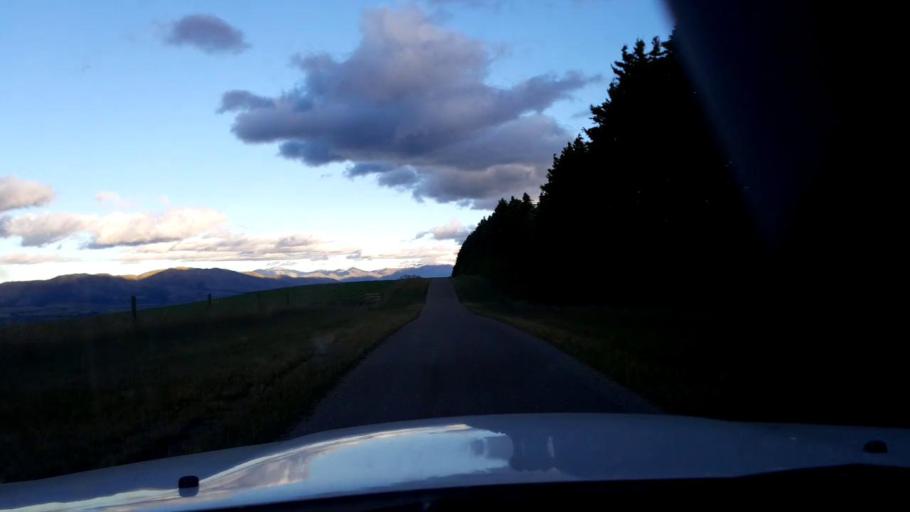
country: NZ
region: Canterbury
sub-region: Timaru District
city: Pleasant Point
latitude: -44.2613
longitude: 170.9173
